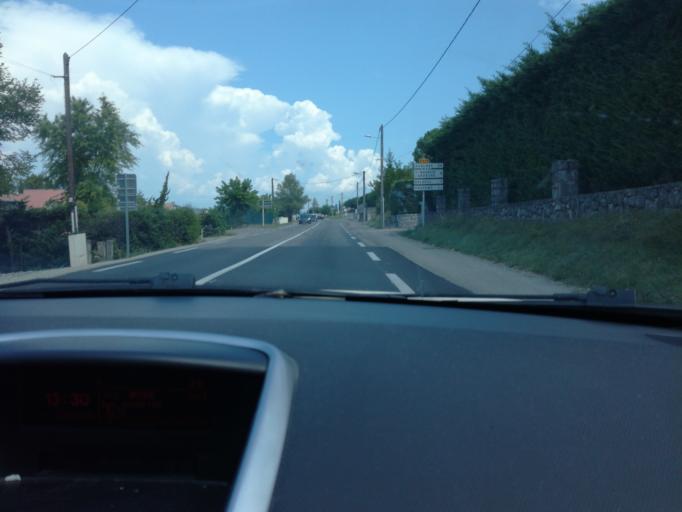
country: FR
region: Rhone-Alpes
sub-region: Departement de l'Ardeche
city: Ruoms
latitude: 44.4619
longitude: 4.3440
